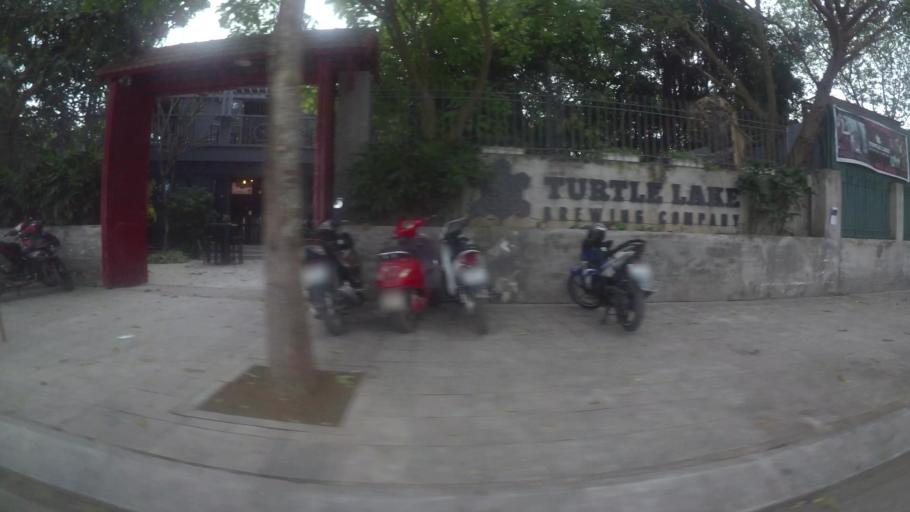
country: VN
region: Ha Noi
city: Tay Ho
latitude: 21.0594
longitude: 105.8186
